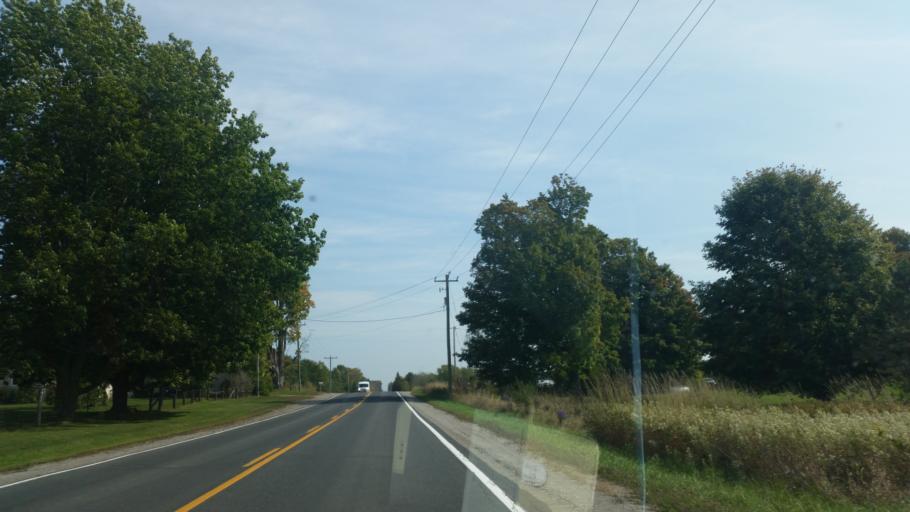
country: CA
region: Ontario
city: Orillia
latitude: 44.6353
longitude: -79.1881
